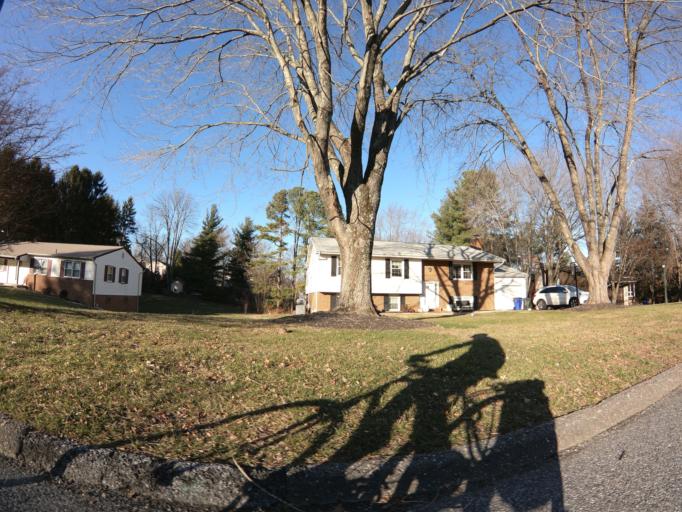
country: US
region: Maryland
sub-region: Howard County
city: Columbia
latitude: 39.2521
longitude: -76.8613
